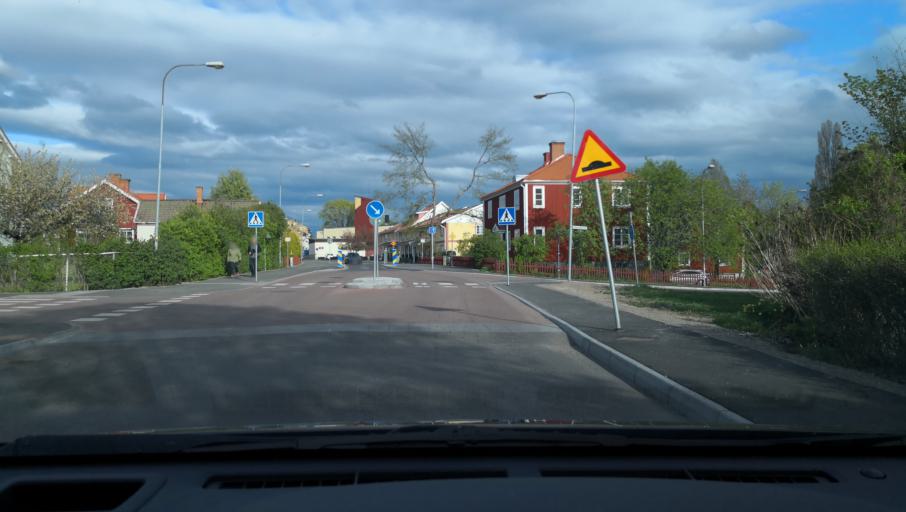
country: SE
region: Dalarna
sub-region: Hedemora Kommun
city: Hedemora
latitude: 60.2784
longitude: 15.9776
